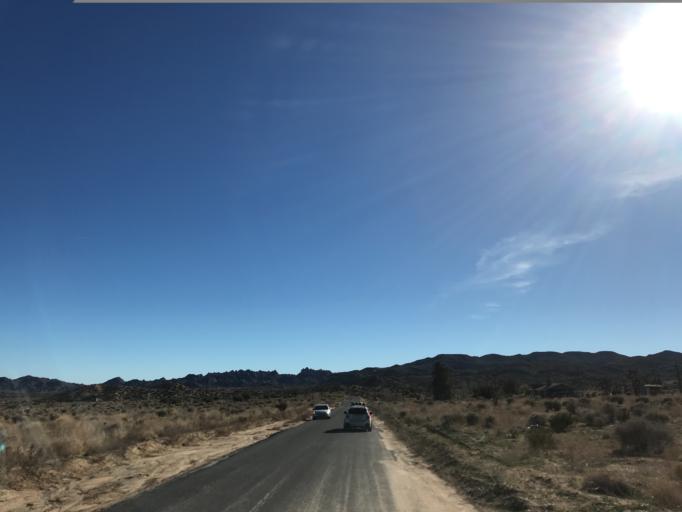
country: US
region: California
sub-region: San Bernardino County
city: Yucca Valley
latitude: 34.1979
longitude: -116.5461
